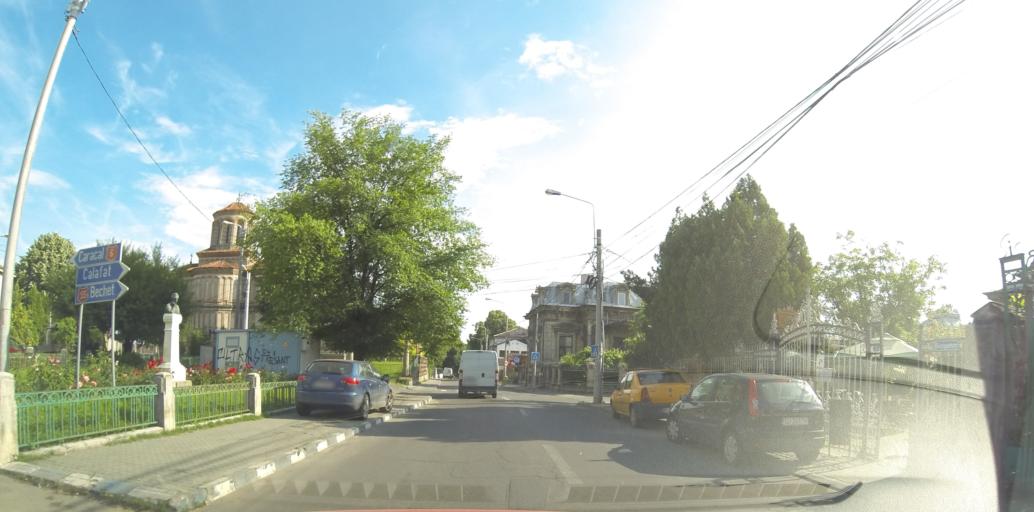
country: RO
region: Dolj
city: Craiova
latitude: 44.3144
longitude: 23.7993
